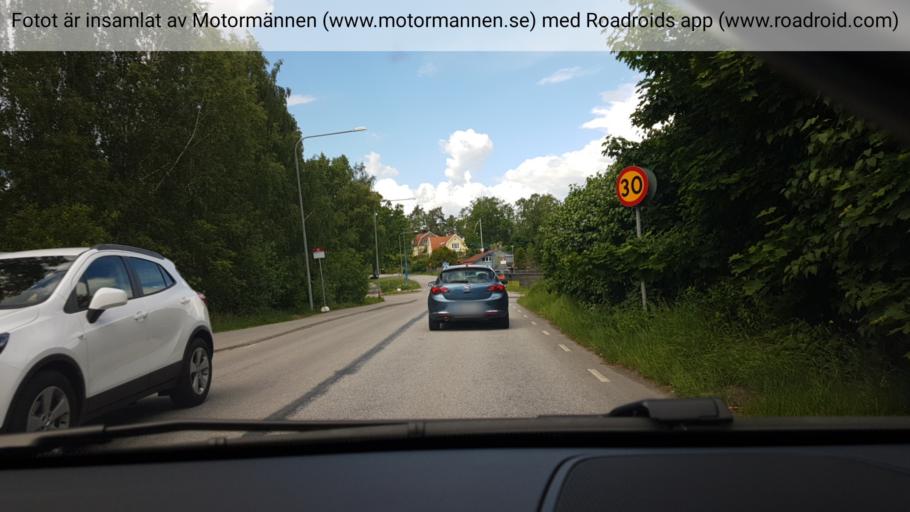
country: SE
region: Stockholm
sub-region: Huddinge Kommun
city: Huddinge
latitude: 59.2324
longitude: 17.9976
